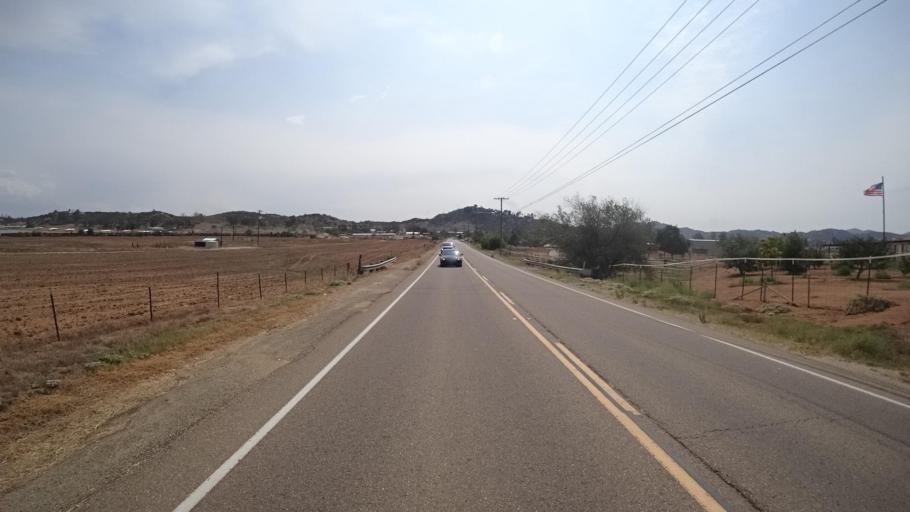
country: US
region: California
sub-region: San Diego County
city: Ramona
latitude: 33.0137
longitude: -116.8795
